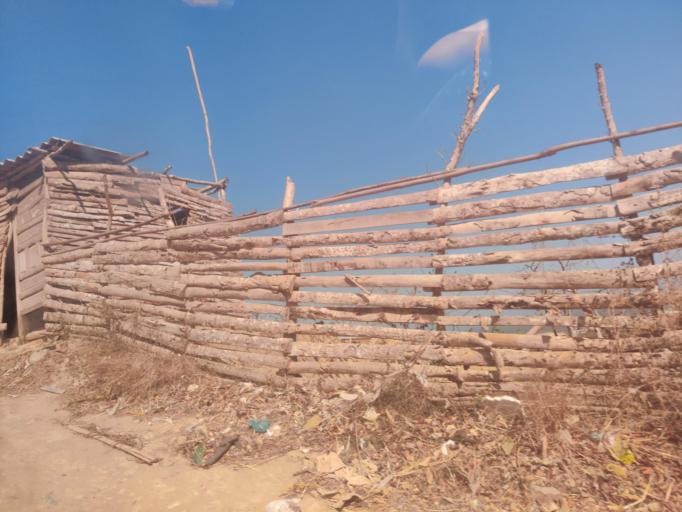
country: CO
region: Atlantico
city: Puerto Colombia
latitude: 10.9790
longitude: -74.9546
